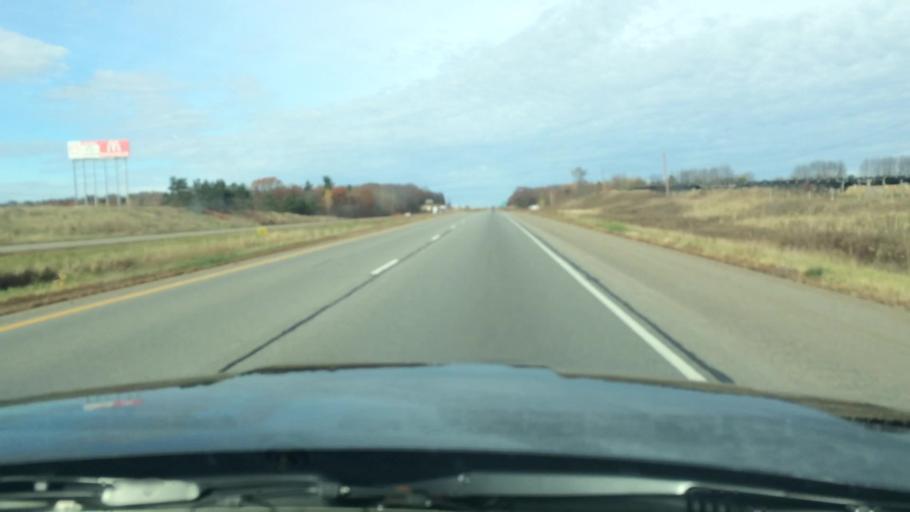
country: US
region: Wisconsin
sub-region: Marathon County
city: Mosinee
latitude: 44.7577
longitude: -89.6798
